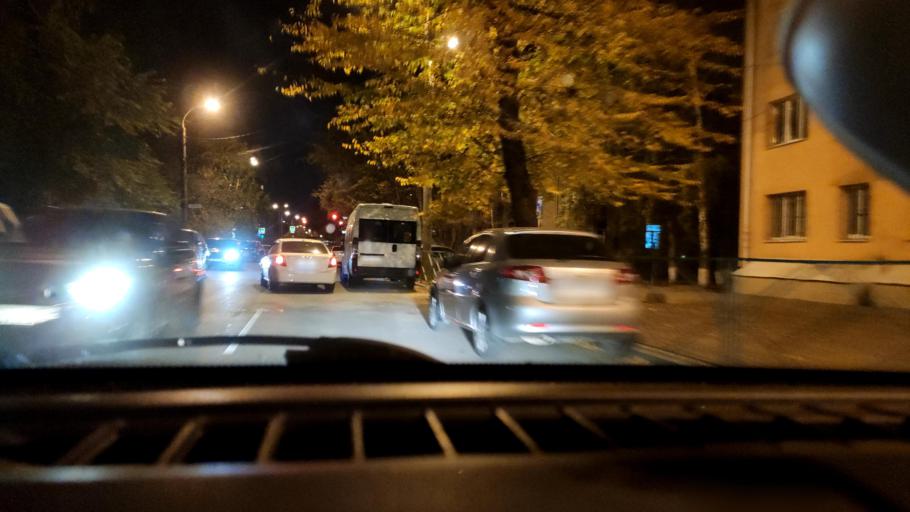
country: RU
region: Samara
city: Samara
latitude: 53.2325
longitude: 50.2485
